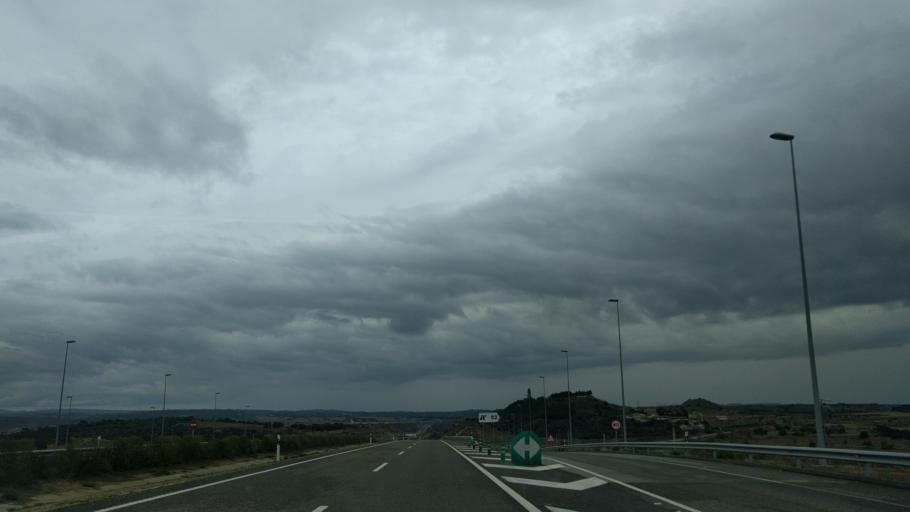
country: ES
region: Aragon
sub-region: Provincia de Huesca
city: Castejon del Puente
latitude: 41.9720
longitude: 0.1479
